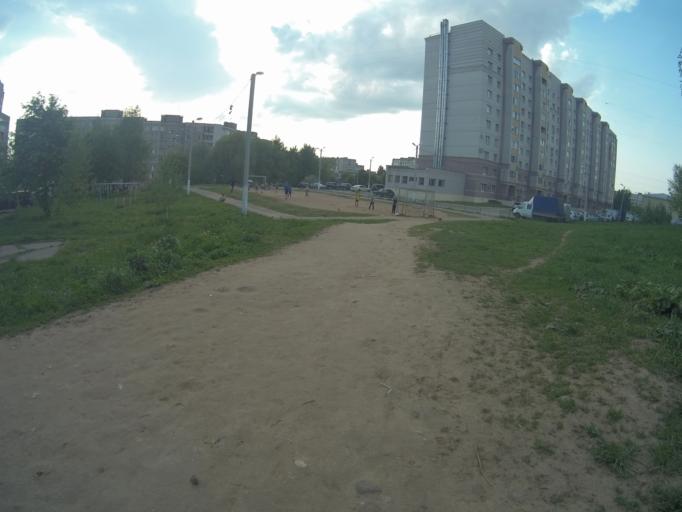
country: RU
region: Vladimir
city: Kommunar
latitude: 56.1680
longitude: 40.4428
